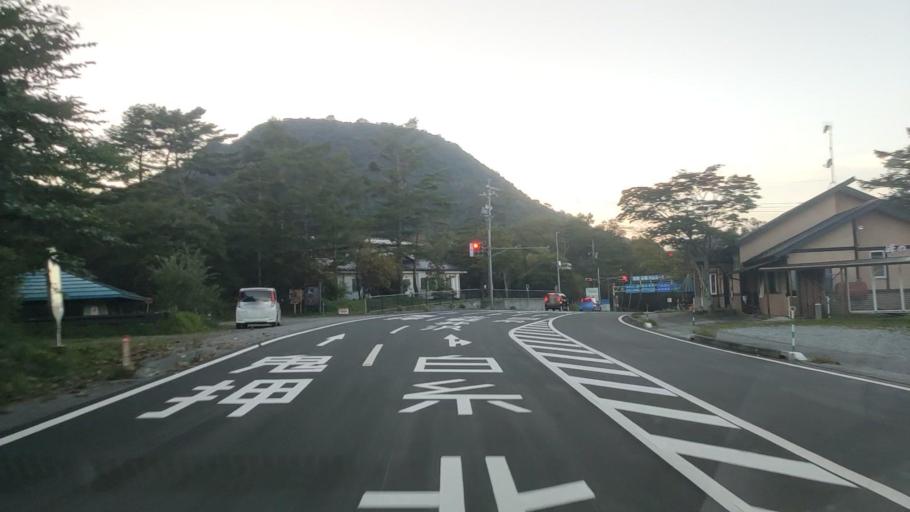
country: JP
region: Nagano
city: Komoro
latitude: 36.4040
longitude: 138.5695
